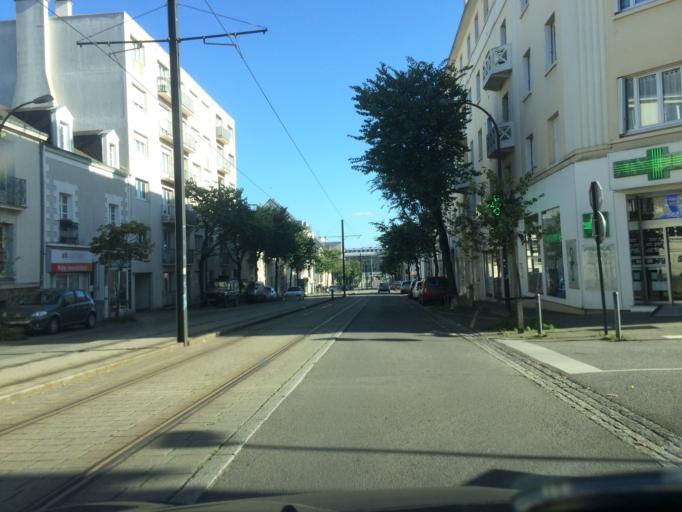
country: FR
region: Pays de la Loire
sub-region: Departement de la Loire-Atlantique
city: Nantes
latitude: 47.2301
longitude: -1.5557
